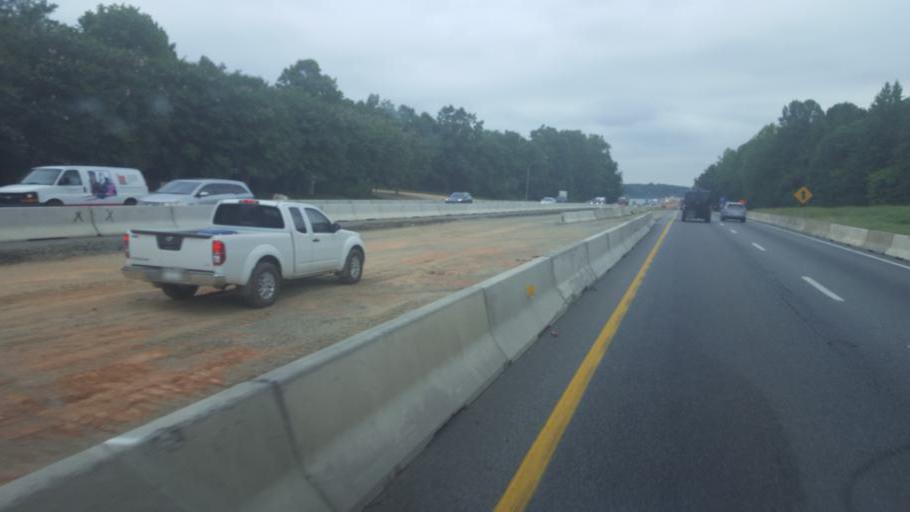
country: US
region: North Carolina
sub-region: Mecklenburg County
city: Cornelius
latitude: 35.5041
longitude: -80.8663
